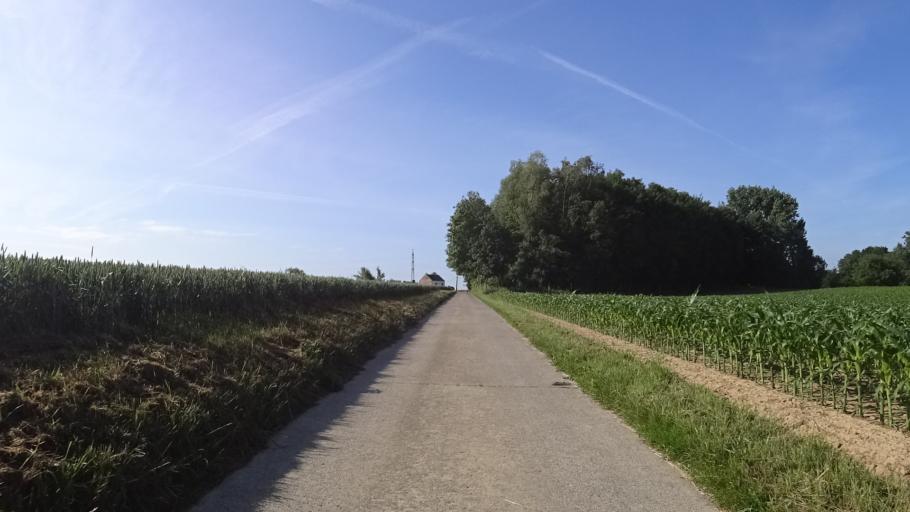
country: BE
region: Wallonia
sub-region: Province de Namur
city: Namur
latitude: 50.5253
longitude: 4.8353
